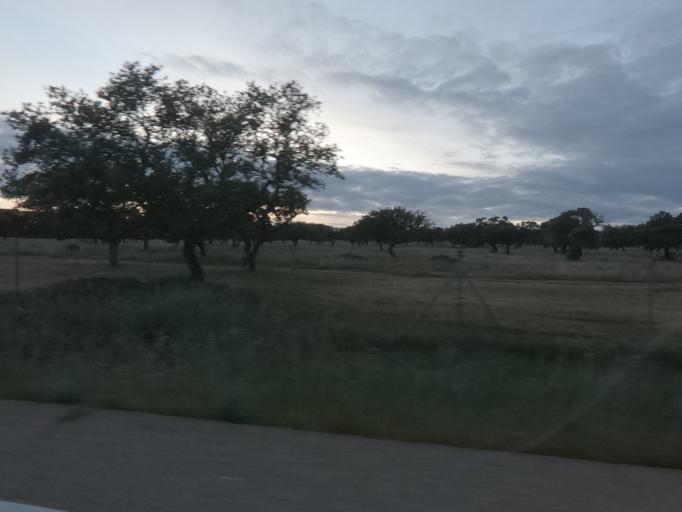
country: ES
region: Extremadura
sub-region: Provincia de Badajoz
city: Villar del Rey
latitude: 39.0025
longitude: -6.8639
